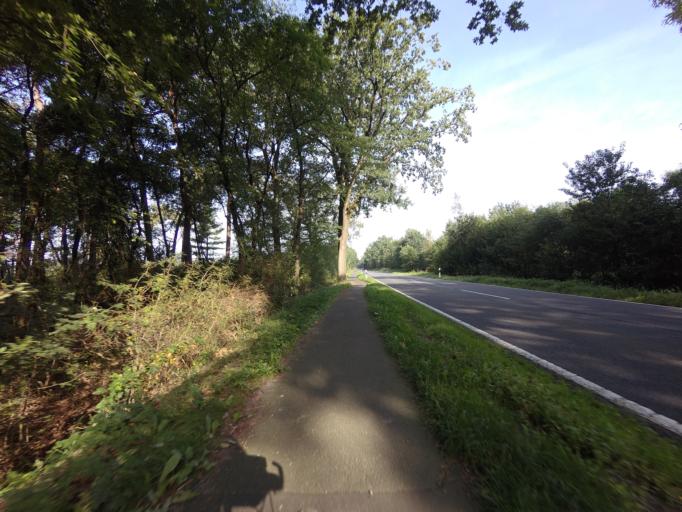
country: DE
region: Lower Saxony
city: Wielen
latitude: 52.5345
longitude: 6.7091
